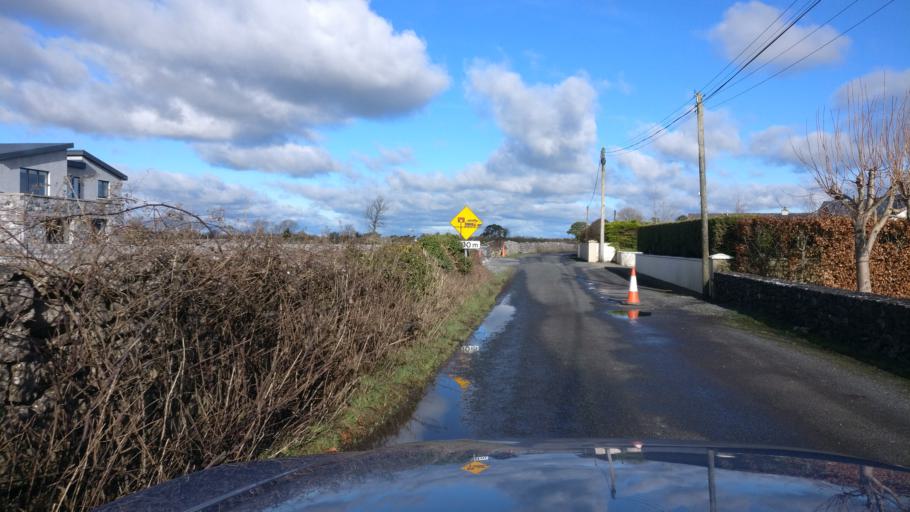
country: IE
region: Connaught
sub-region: County Galway
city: Oranmore
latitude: 53.2792
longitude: -8.9038
